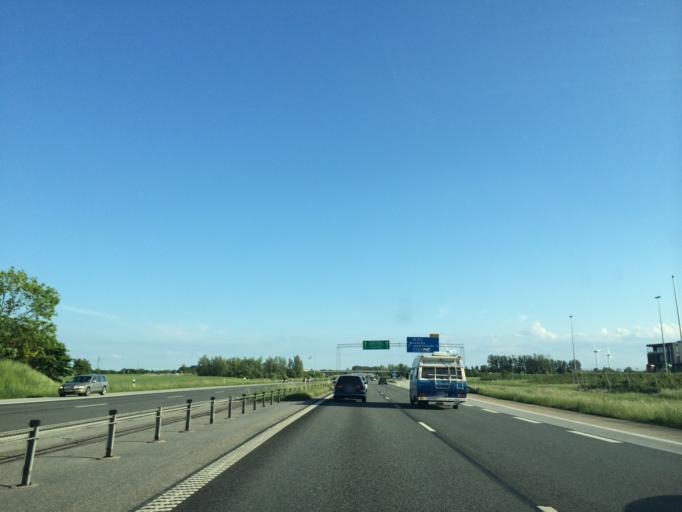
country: SE
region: Skane
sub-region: Landskrona
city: Landskrona
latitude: 55.8803
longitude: 12.8779
